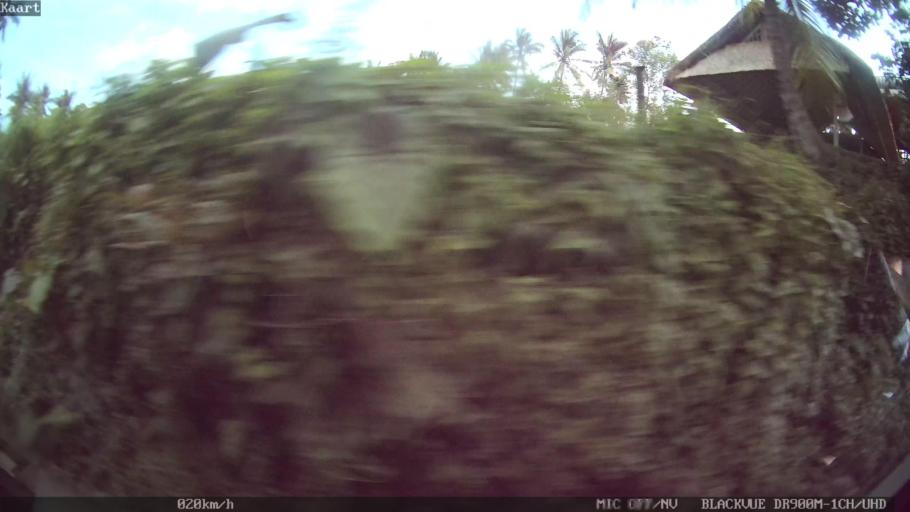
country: ID
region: Bali
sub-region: Kabupaten Gianyar
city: Ubud
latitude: -8.5095
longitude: 115.2769
